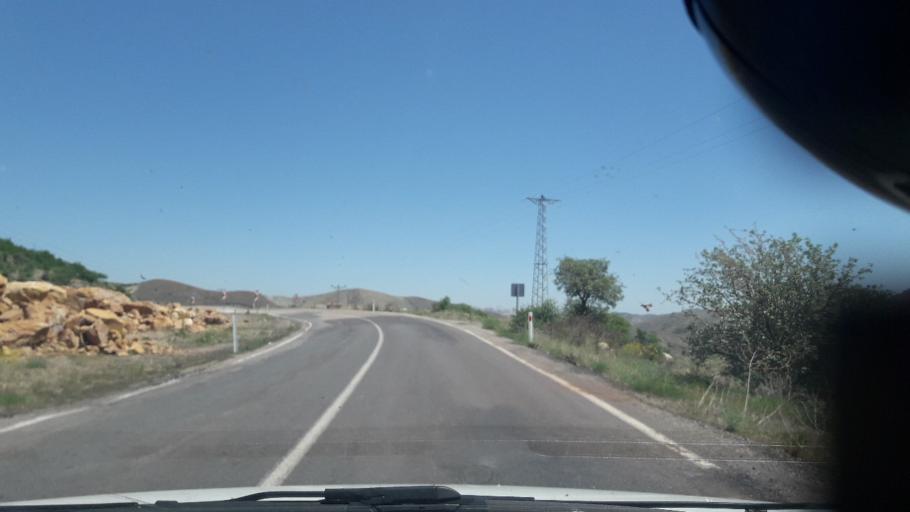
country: TR
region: Malatya
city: Hekimhan
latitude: 38.8402
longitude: 37.8330
